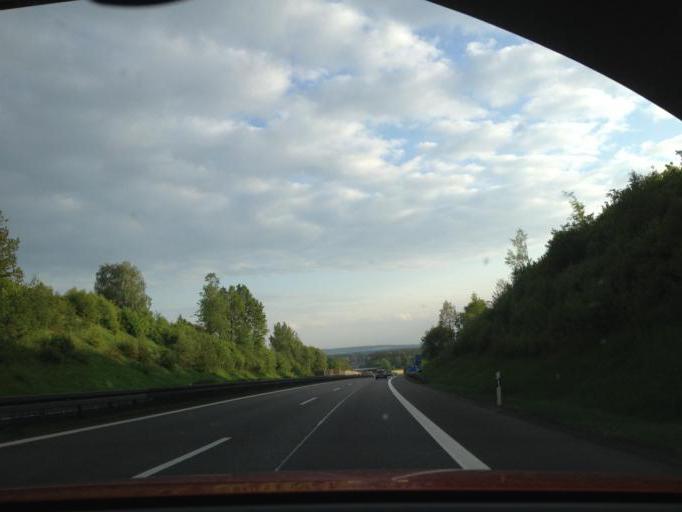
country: DE
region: Bavaria
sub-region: Upper Palatinate
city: Neustadt an der Waldnaab
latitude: 49.7279
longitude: 12.1558
